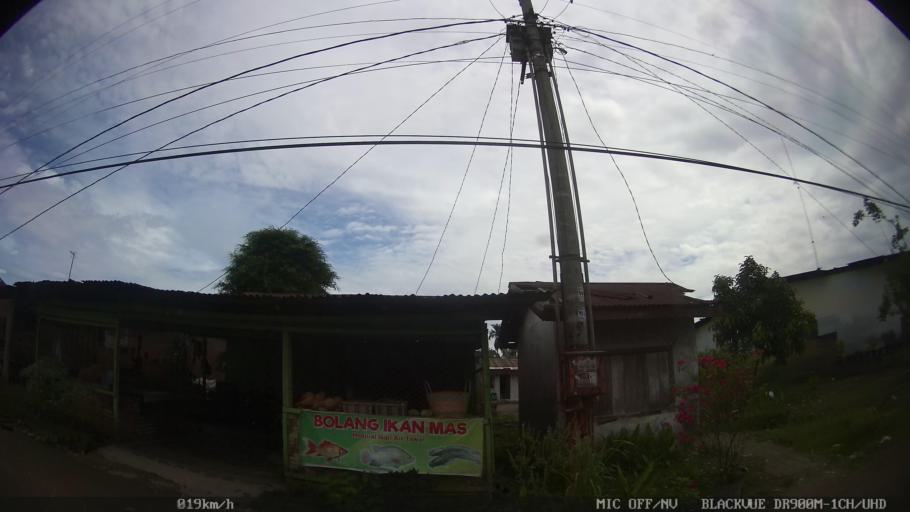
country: ID
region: North Sumatra
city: Sunggal
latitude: 3.5910
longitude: 98.5669
